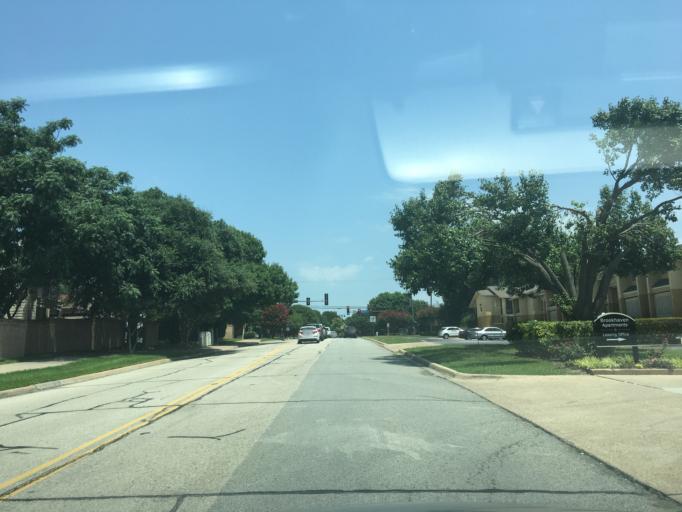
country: US
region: Texas
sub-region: Dallas County
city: Addison
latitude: 32.9496
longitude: -96.8582
